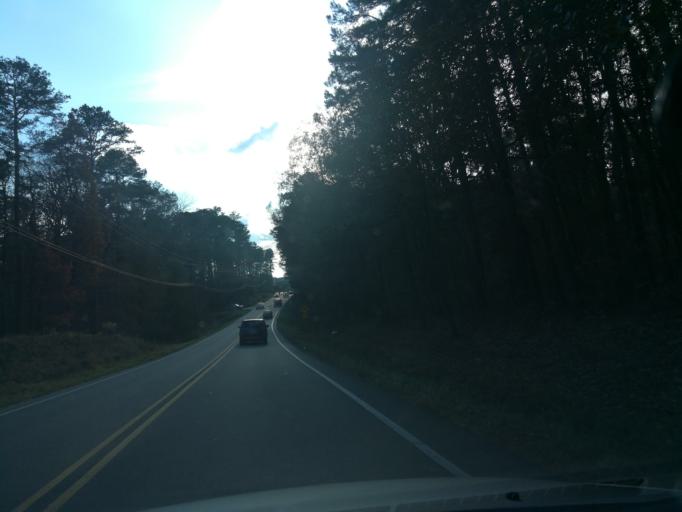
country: US
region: North Carolina
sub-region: Orange County
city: Chapel Hill
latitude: 35.9823
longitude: -78.9967
